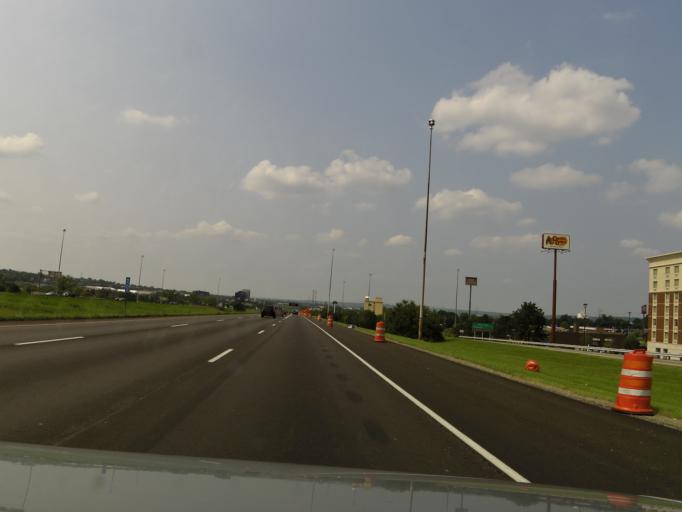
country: US
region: Ohio
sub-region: Hamilton County
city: Glendale
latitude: 39.2673
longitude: -84.4395
